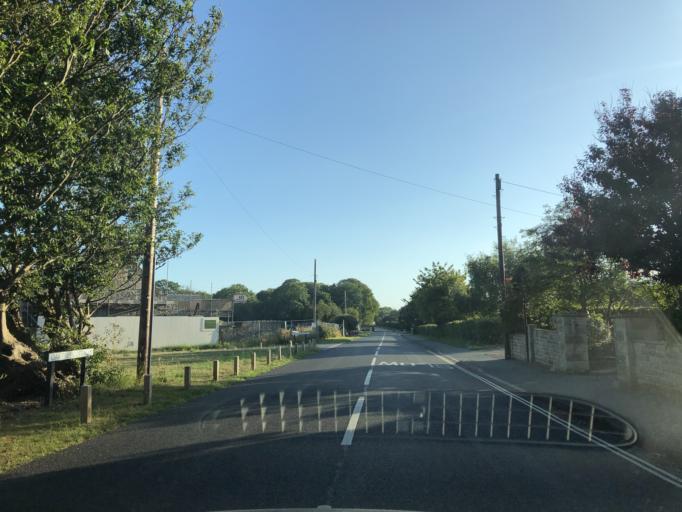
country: GB
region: England
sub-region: Isle of Wight
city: Shalfleet
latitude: 50.6415
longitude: -1.3957
